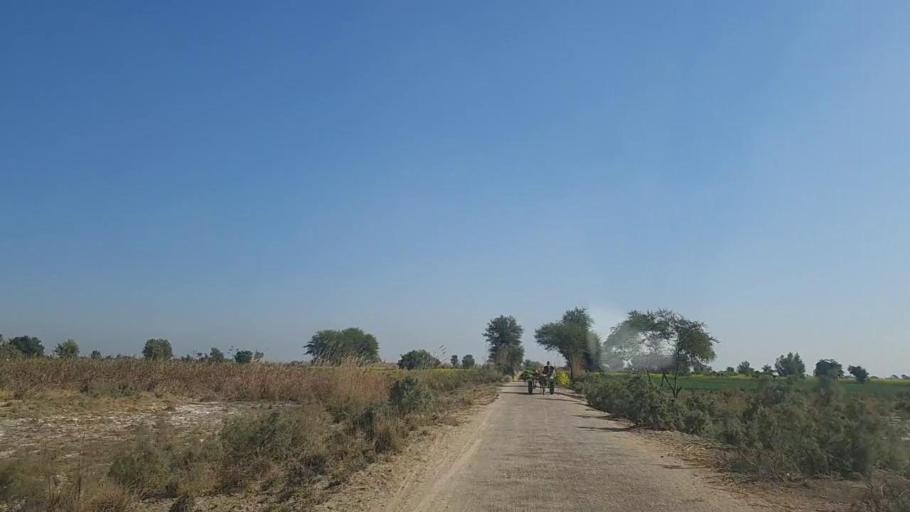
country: PK
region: Sindh
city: Sinjhoro
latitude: 26.1589
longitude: 68.8571
